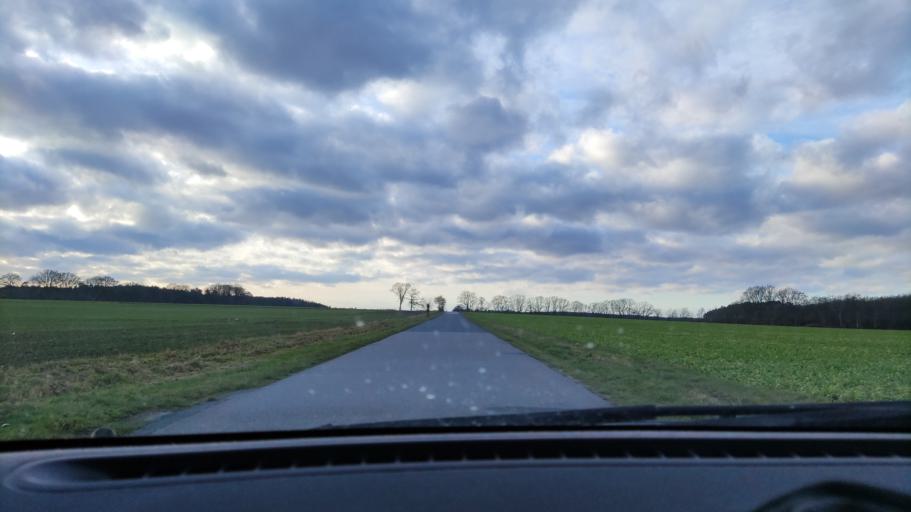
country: DE
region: Lower Saxony
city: Eimke
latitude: 52.9821
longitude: 10.3583
